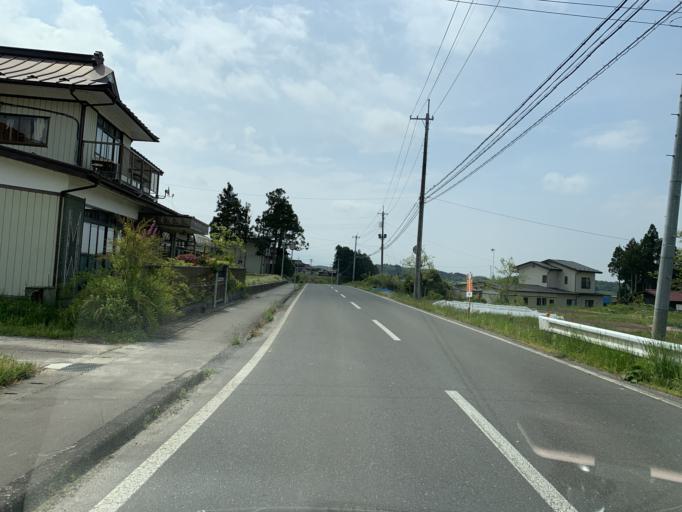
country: JP
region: Iwate
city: Ichinoseki
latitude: 38.8263
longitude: 141.2022
